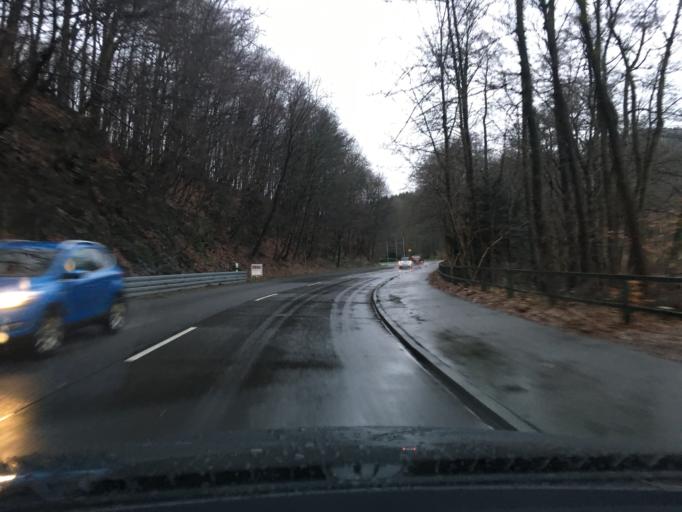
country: DE
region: North Rhine-Westphalia
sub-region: Regierungsbezirk Dusseldorf
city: Velbert
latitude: 51.3199
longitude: 7.0849
